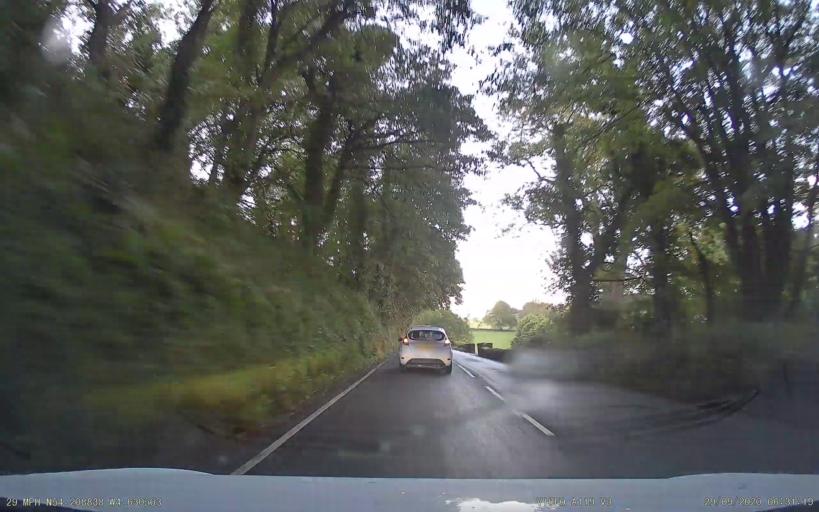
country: IM
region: Castletown
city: Castletown
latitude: 54.2088
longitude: -4.6305
